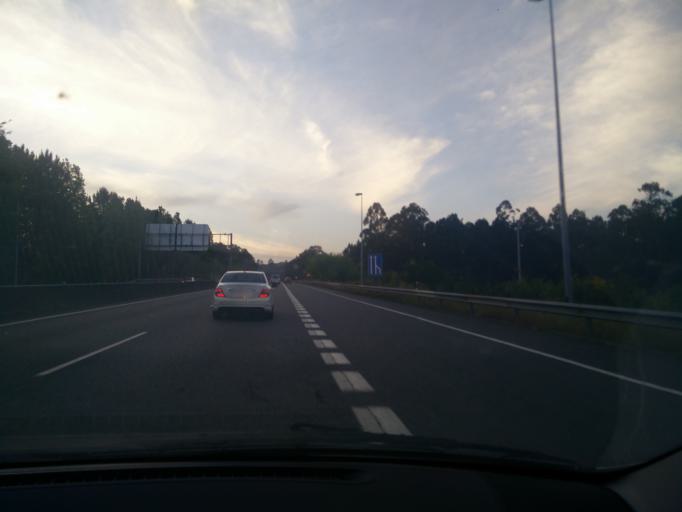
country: ES
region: Galicia
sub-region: Provincia de Pontevedra
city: Porrino
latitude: 42.1743
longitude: -8.6233
